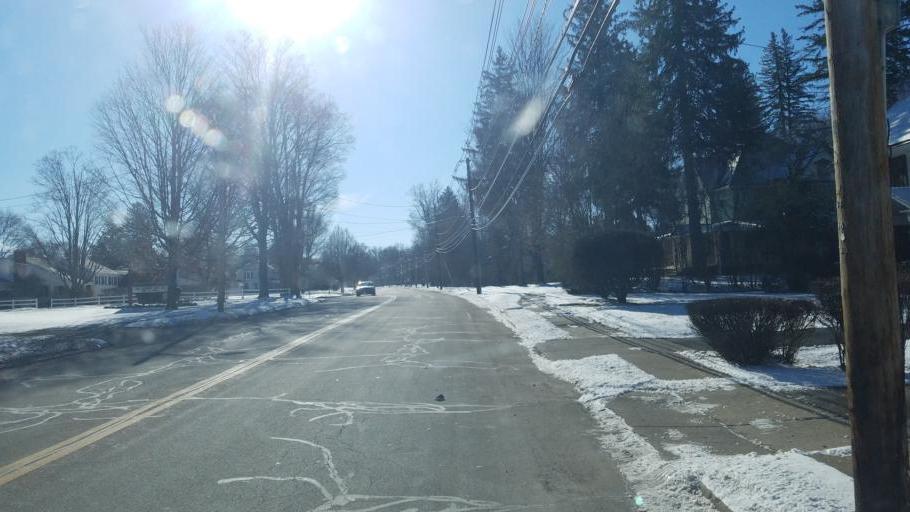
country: US
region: New York
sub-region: Allegany County
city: Wellsville
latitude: 42.1282
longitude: -77.9583
